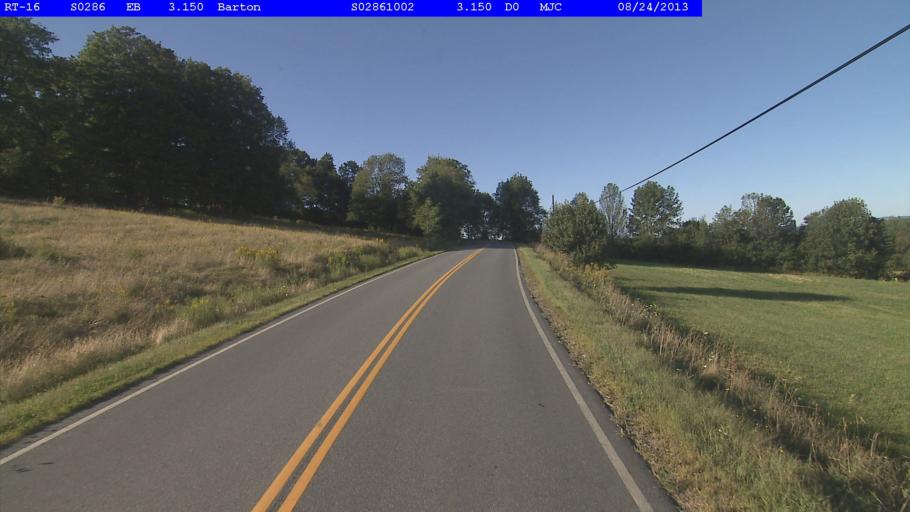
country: US
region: Vermont
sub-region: Orleans County
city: Newport
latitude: 44.7679
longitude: -72.1277
